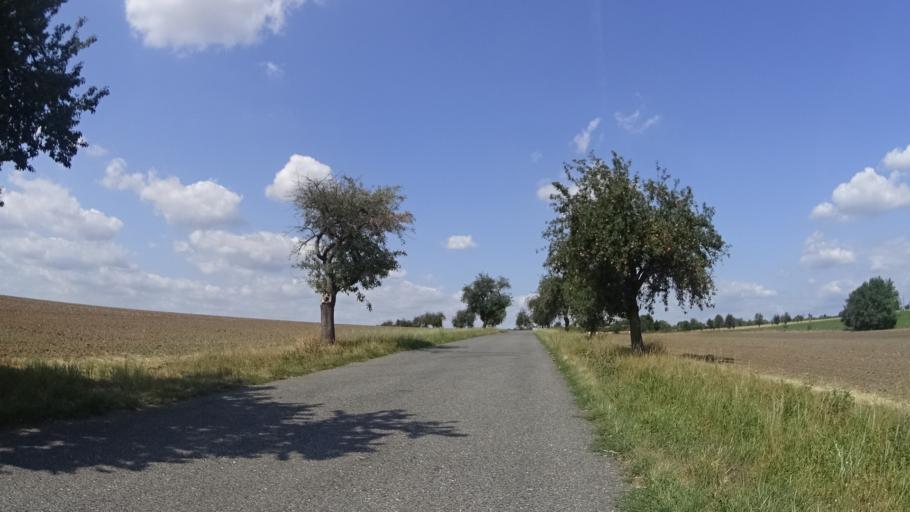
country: CZ
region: Kralovehradecky
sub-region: Okres Jicin
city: Jicin
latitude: 50.3757
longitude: 15.3352
